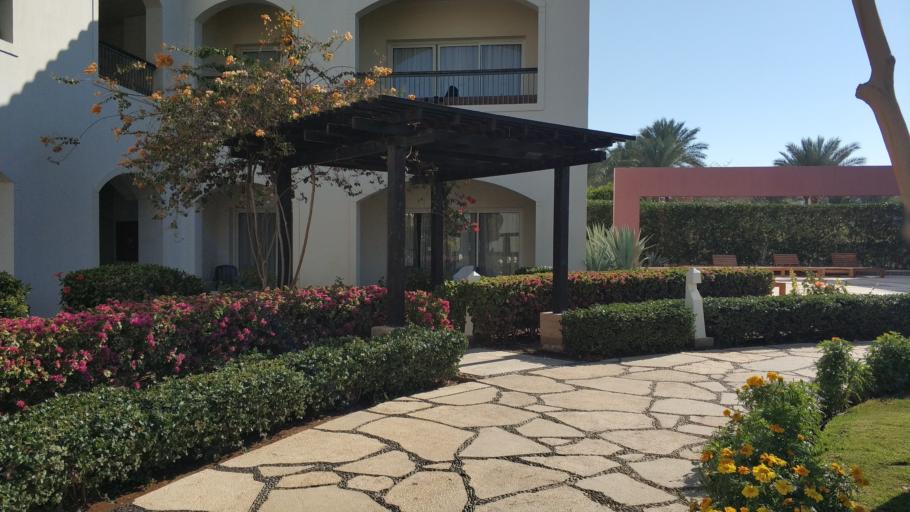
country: EG
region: South Sinai
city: Sharm el-Sheikh
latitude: 27.9205
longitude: 34.3610
